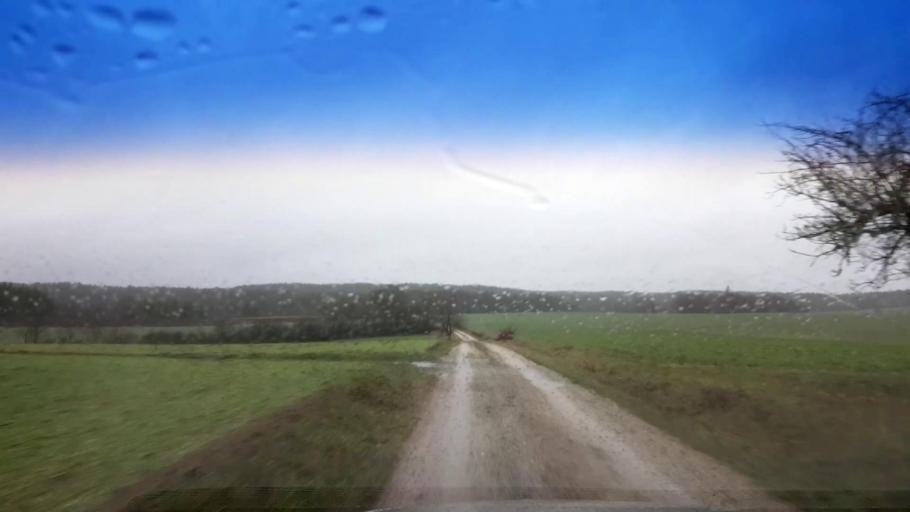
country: DE
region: Bavaria
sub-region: Upper Franconia
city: Lauter
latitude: 49.9488
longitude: 10.7682
